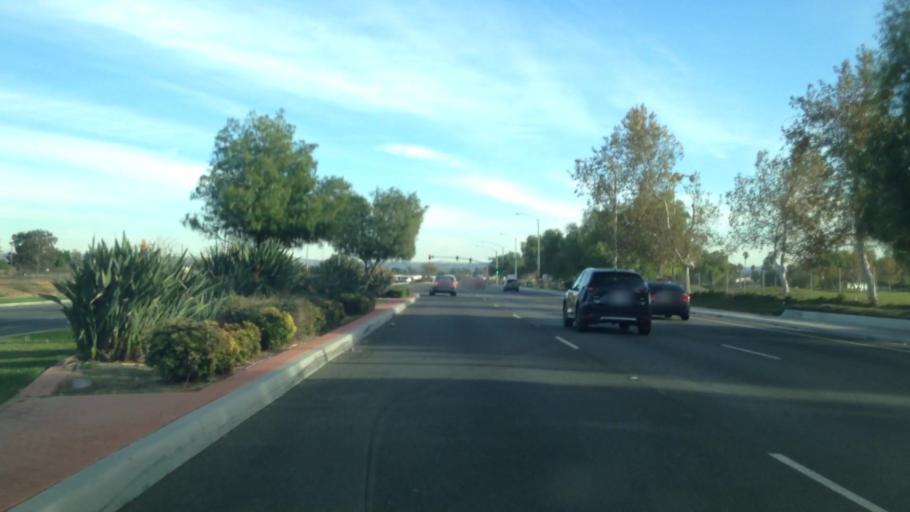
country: US
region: California
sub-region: Riverside County
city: Pedley
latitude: 33.9569
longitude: -117.4591
